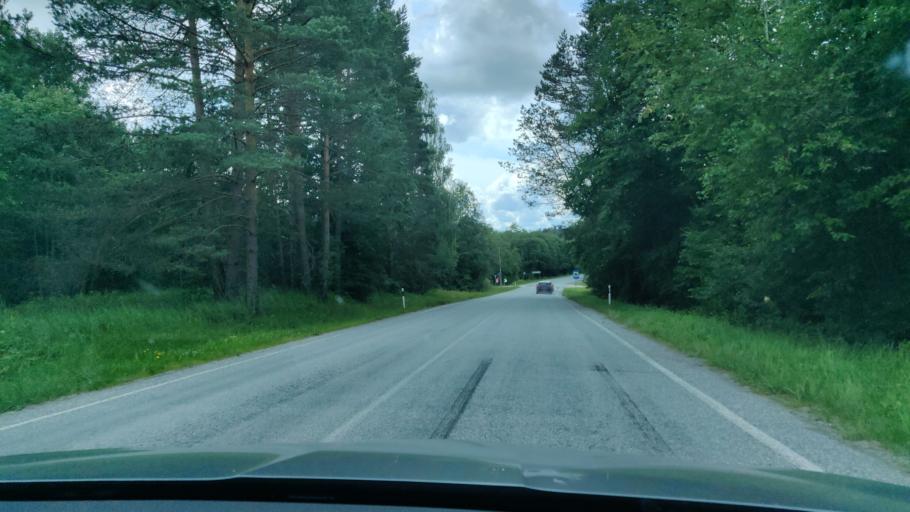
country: EE
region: Vorumaa
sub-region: Antsla vald
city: Vana-Antsla
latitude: 58.0231
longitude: 26.5042
